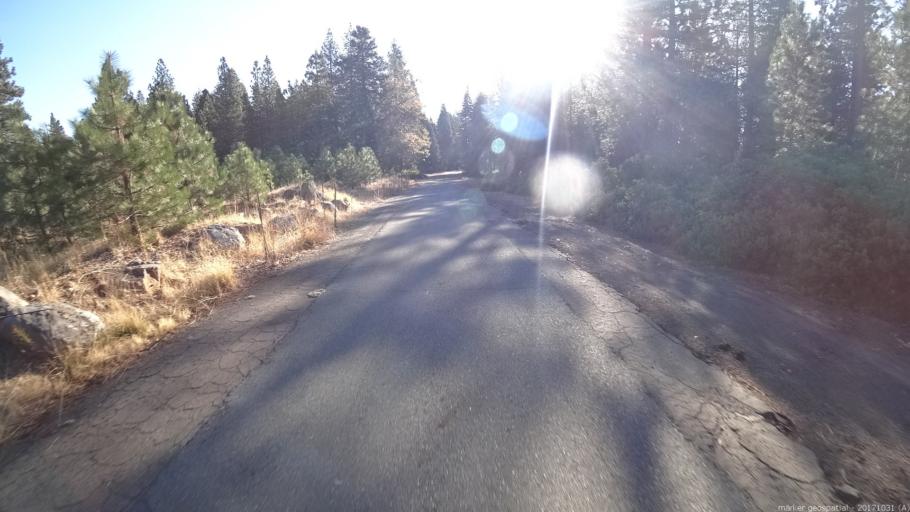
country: US
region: California
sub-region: Shasta County
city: Shingletown
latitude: 40.5185
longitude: -121.8190
